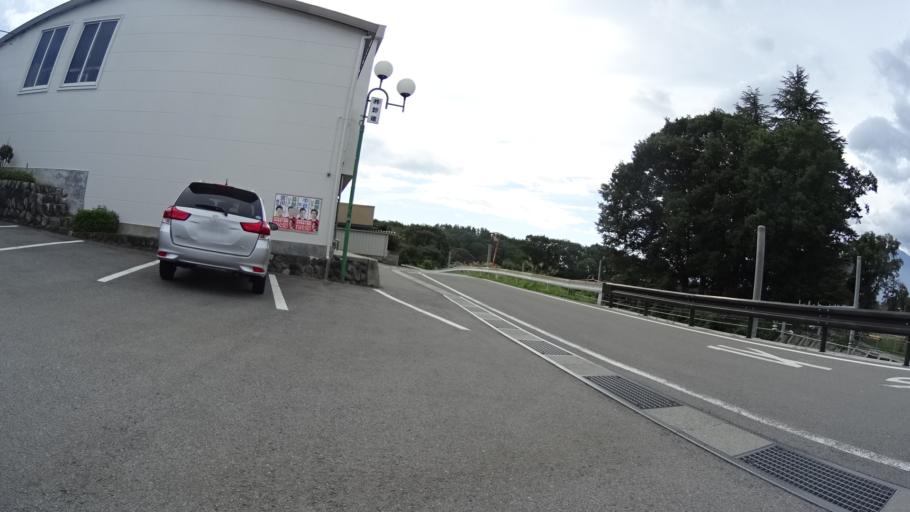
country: JP
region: Yamanashi
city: Nirasaki
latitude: 35.8632
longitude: 138.3197
